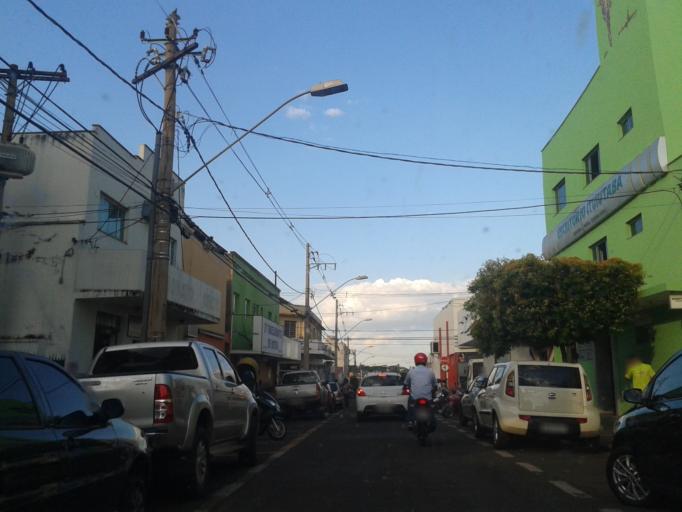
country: BR
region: Minas Gerais
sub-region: Ituiutaba
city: Ituiutaba
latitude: -18.9716
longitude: -49.4637
